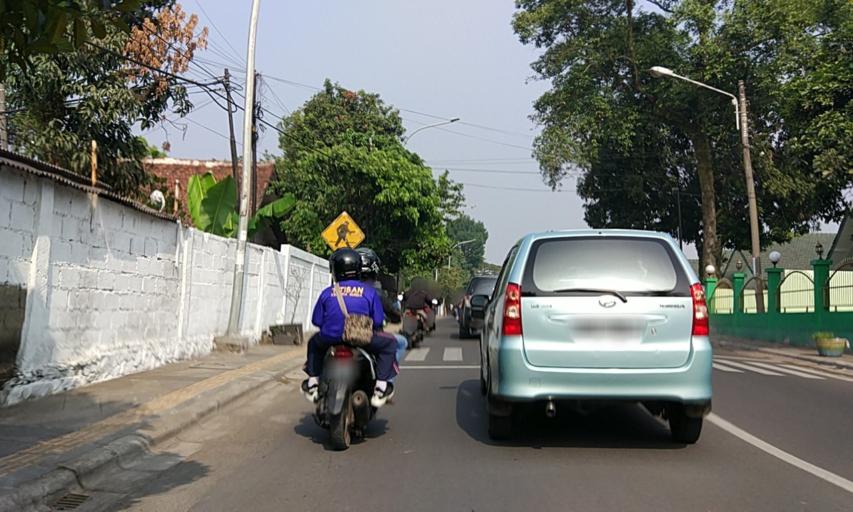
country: ID
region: West Java
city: Bandung
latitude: -6.9021
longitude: 107.6349
